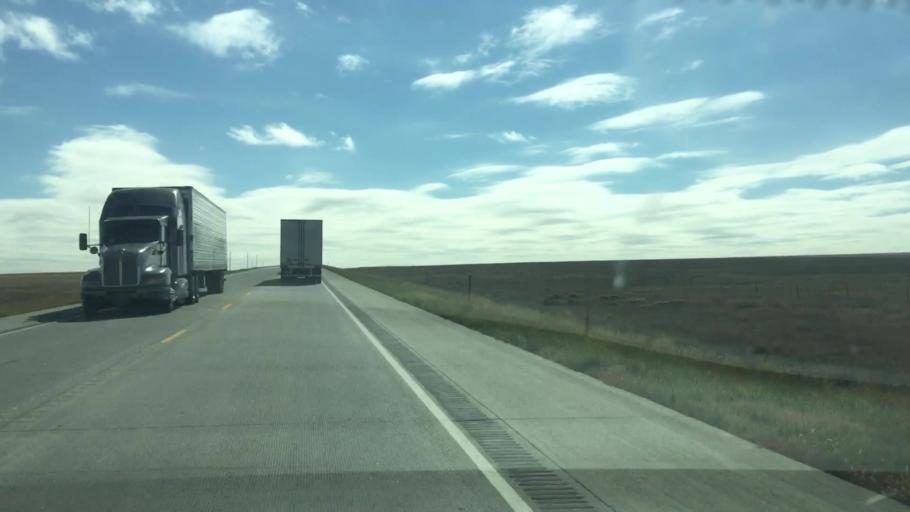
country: US
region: Colorado
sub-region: Lincoln County
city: Hugo
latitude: 39.0265
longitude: -103.3190
